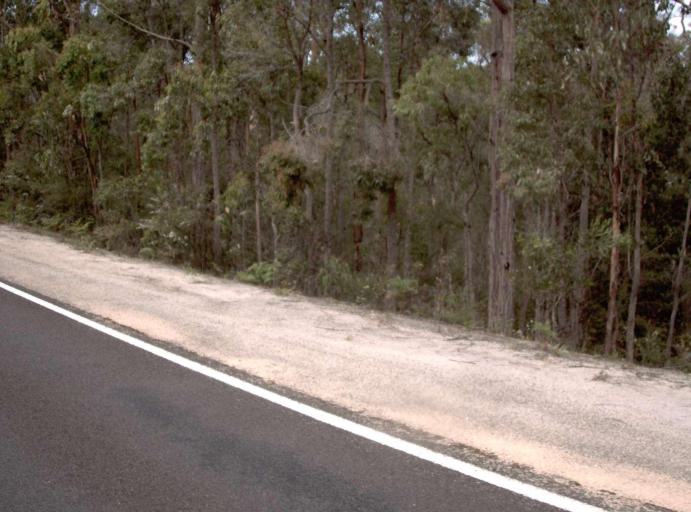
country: AU
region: New South Wales
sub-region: Bega Valley
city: Eden
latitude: -37.4174
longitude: 149.6521
